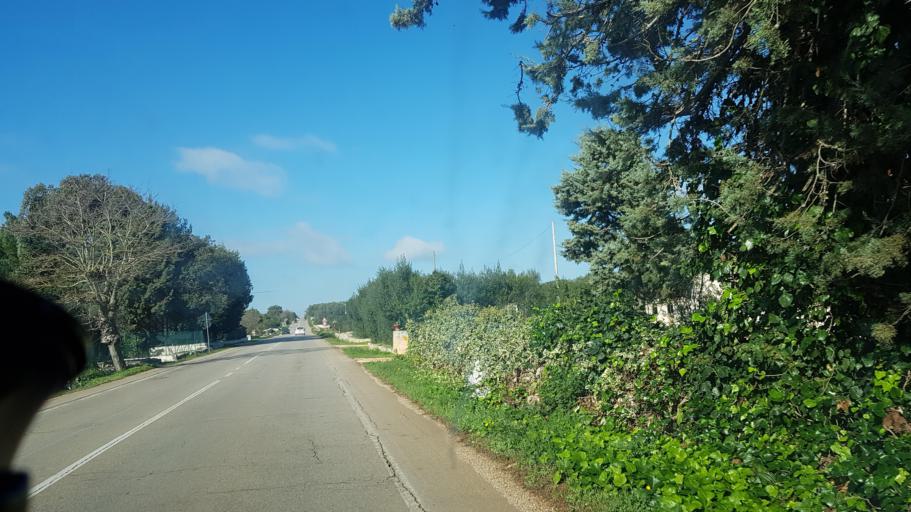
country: IT
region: Apulia
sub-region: Provincia di Brindisi
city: Carovigno
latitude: 40.6829
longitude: 17.6814
